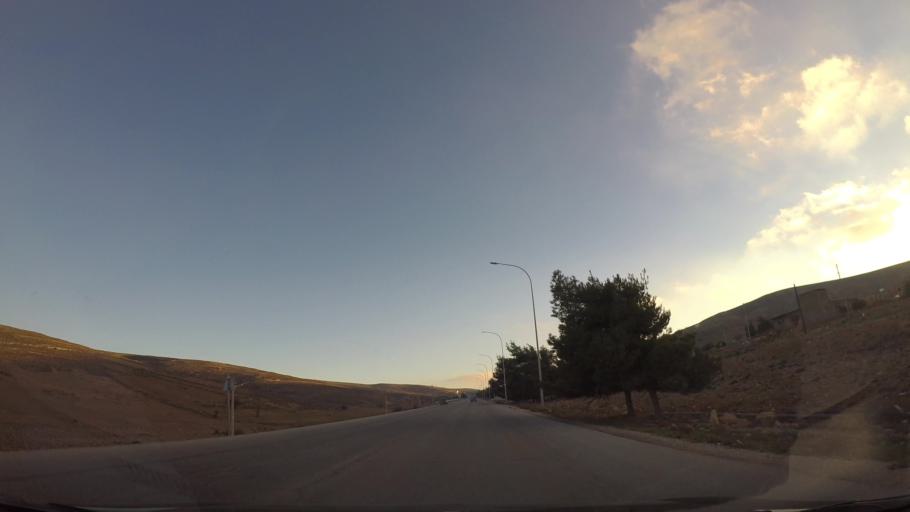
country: JO
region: Ma'an
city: Petra
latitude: 30.4311
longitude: 35.5156
